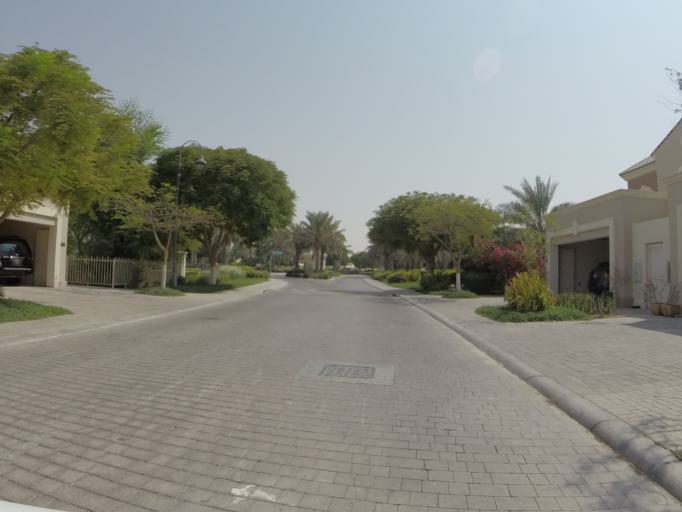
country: AE
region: Dubai
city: Dubai
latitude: 25.0327
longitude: 55.2190
